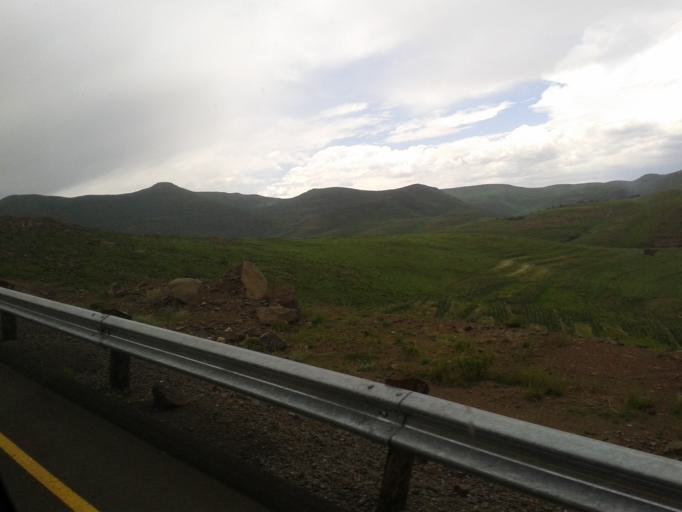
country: LS
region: Maseru
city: Nako
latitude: -29.8188
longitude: 28.0336
